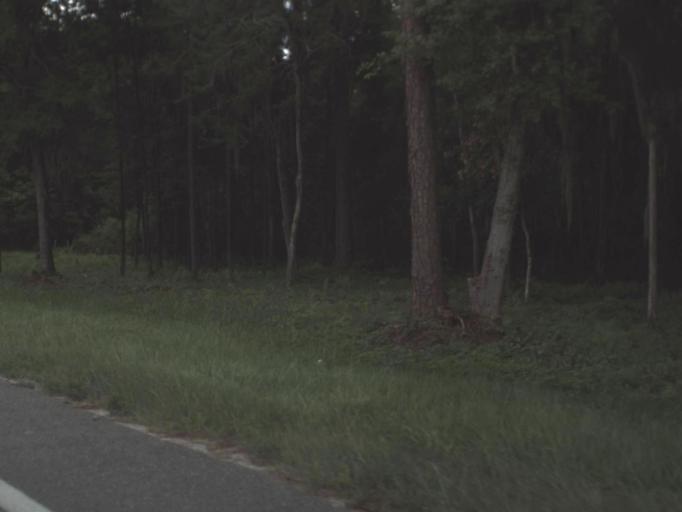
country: US
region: Florida
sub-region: Hamilton County
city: Jasper
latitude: 30.5243
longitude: -82.9843
